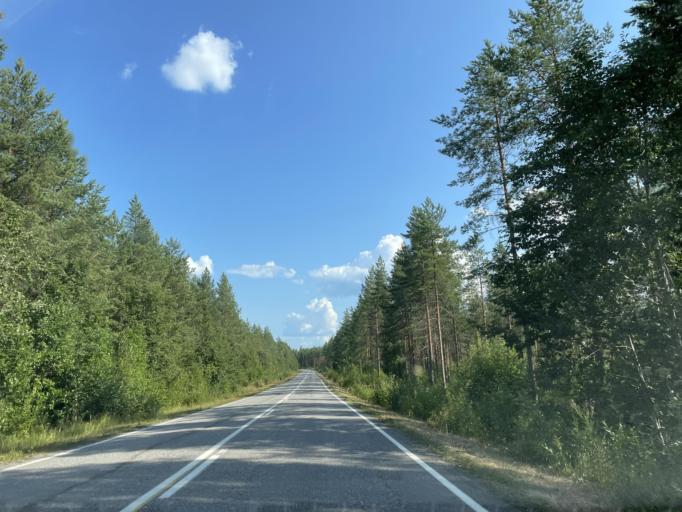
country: FI
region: Central Finland
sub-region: Saarijaervi-Viitasaari
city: Pihtipudas
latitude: 63.3647
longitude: 25.7146
